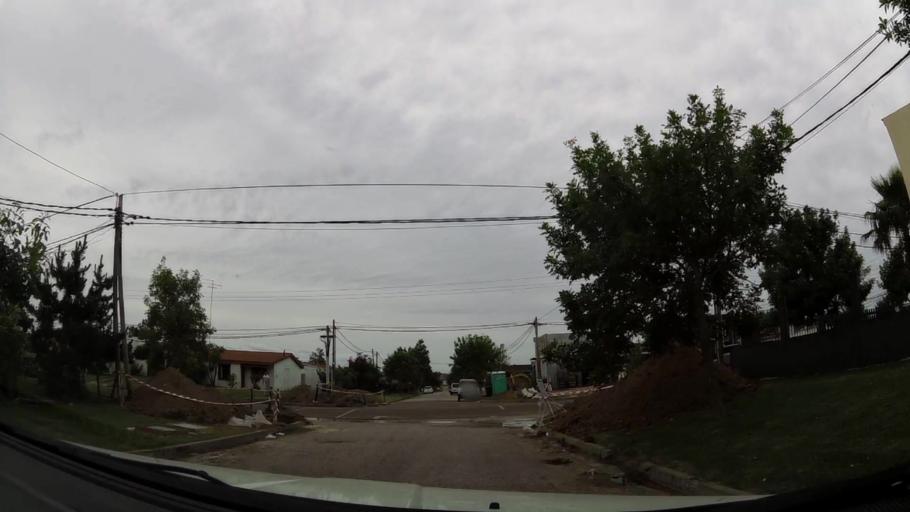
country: UY
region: Maldonado
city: Maldonado
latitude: -34.8885
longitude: -54.9438
